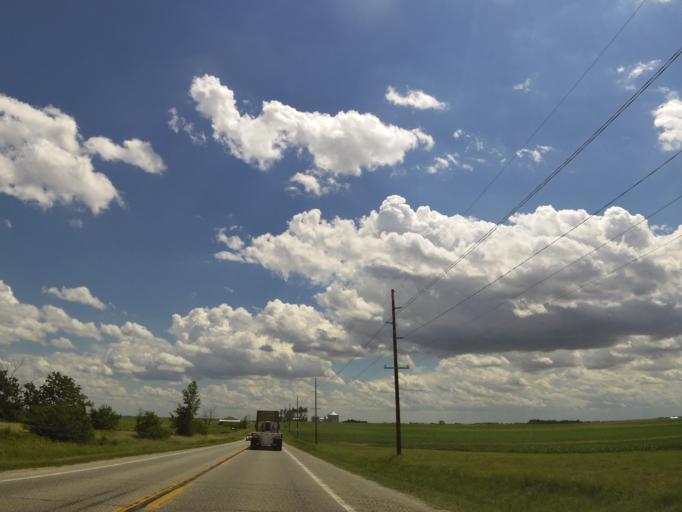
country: US
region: Iowa
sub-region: Benton County
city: Urbana
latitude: 42.2922
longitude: -91.8897
